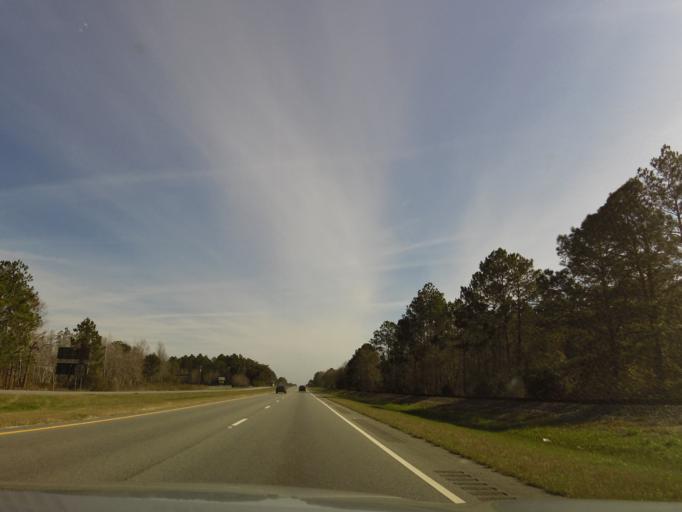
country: US
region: Georgia
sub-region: Lowndes County
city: Valdosta
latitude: 30.8512
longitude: -83.2246
